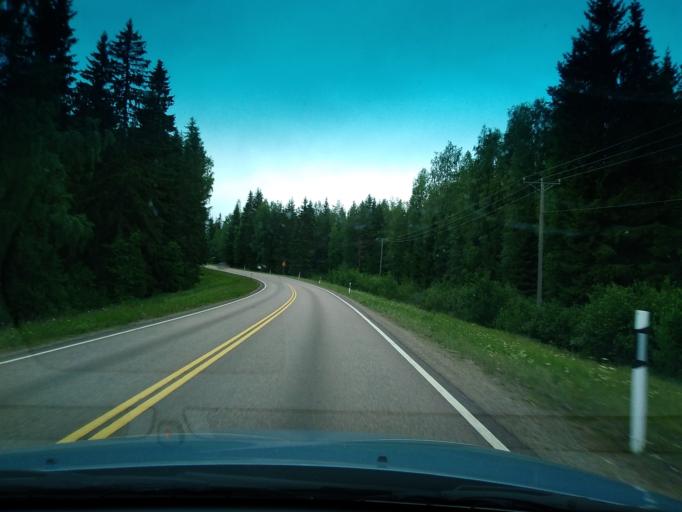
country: FI
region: Central Finland
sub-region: Keuruu
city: Multia
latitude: 62.3925
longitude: 24.7693
